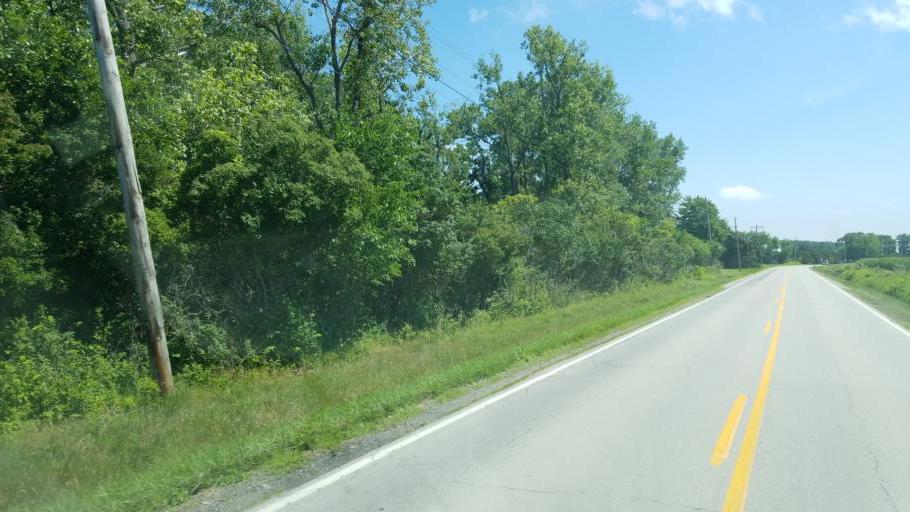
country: US
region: Ohio
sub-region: Erie County
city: Sandusky
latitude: 41.4462
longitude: -82.8140
